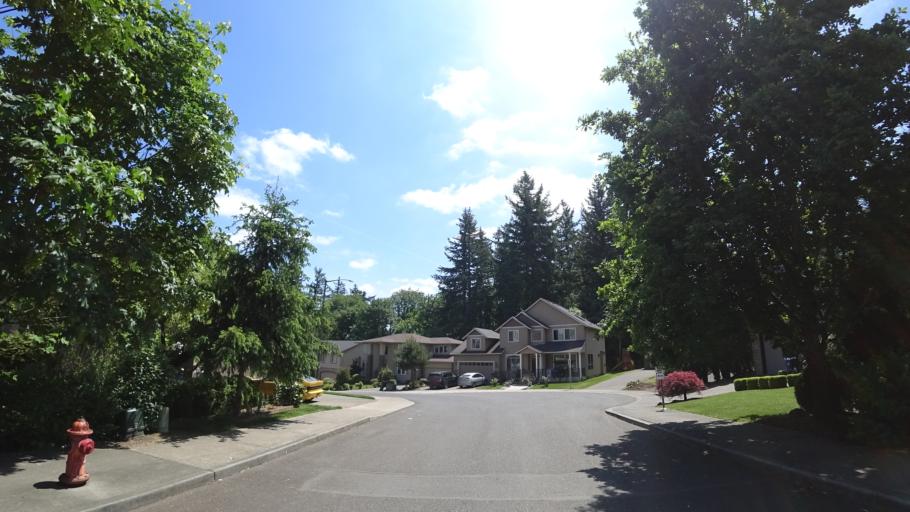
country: US
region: Oregon
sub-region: Clackamas County
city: Happy Valley
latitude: 45.4869
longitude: -122.4941
